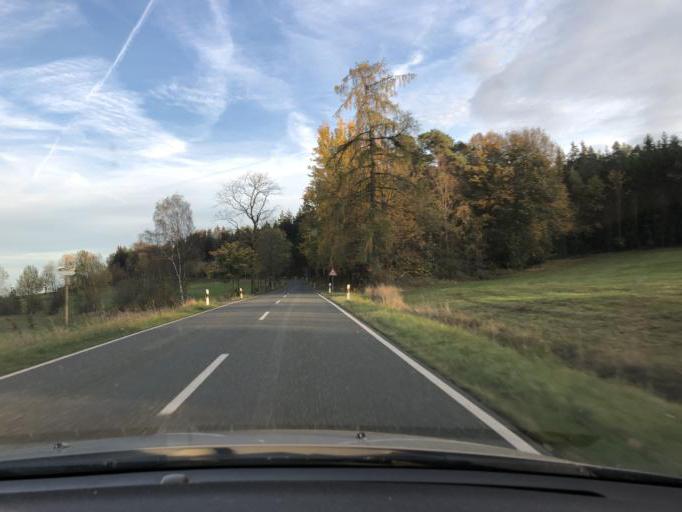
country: DE
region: Thuringia
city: Schleusingen
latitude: 50.4823
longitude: 10.7517
